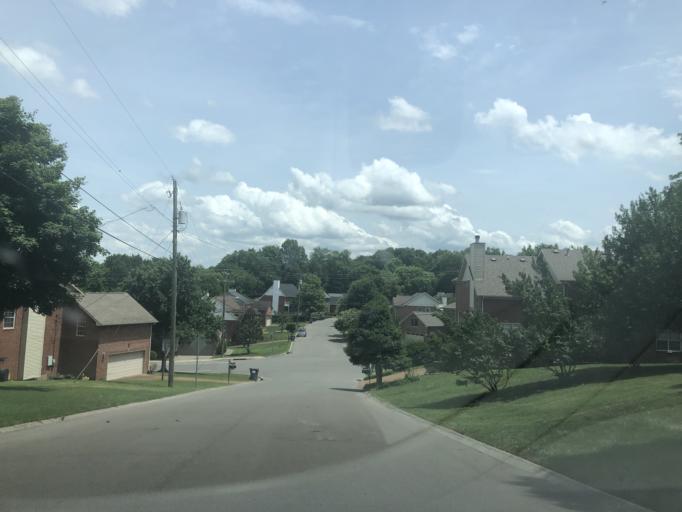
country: US
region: Tennessee
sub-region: Cheatham County
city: Pegram
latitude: 36.0509
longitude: -86.9607
